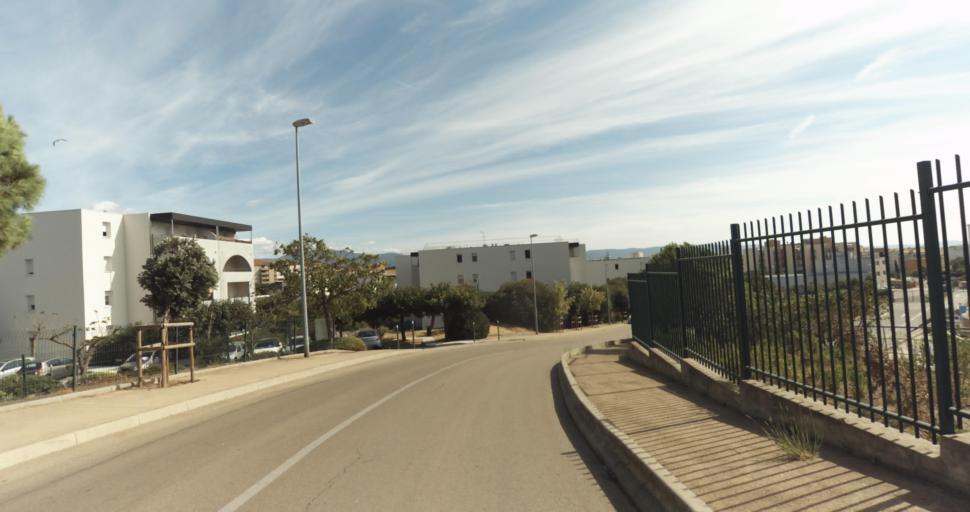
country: FR
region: Corsica
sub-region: Departement de la Corse-du-Sud
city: Ajaccio
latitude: 41.9433
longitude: 8.7470
